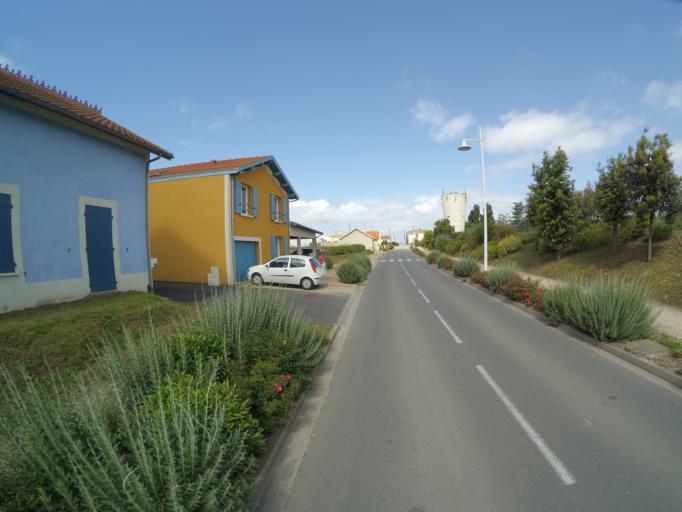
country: FR
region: Poitou-Charentes
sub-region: Departement de la Charente-Maritime
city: Chatelaillon-Plage
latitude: 46.0581
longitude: -1.0850
